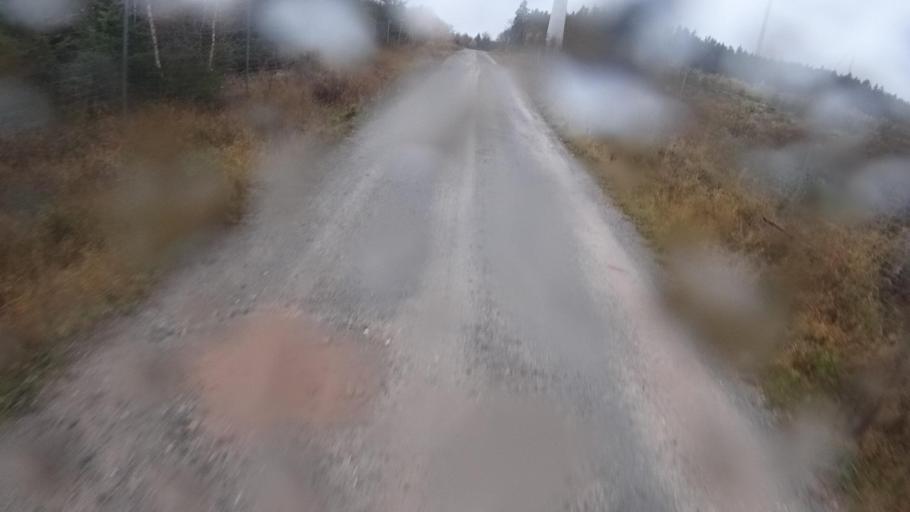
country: DE
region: Rheinland-Pfalz
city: Badenhard
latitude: 50.1017
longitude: 7.6261
